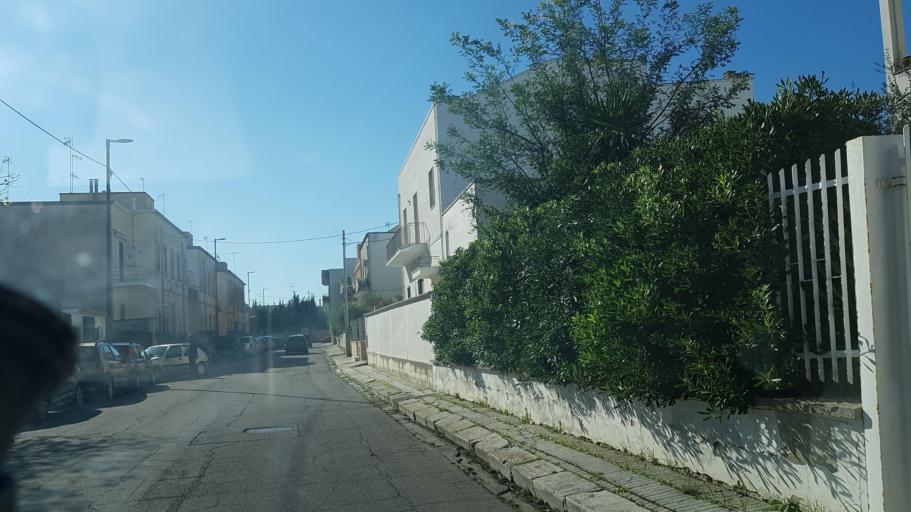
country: IT
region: Apulia
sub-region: Provincia di Lecce
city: Arnesano
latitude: 40.3396
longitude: 18.0897
